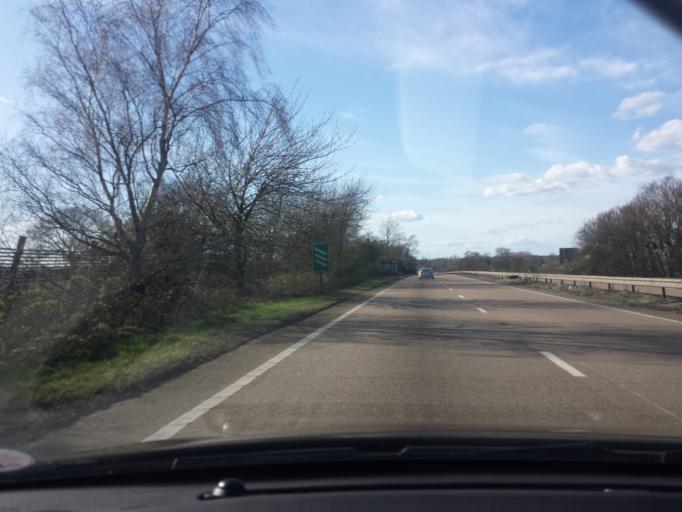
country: GB
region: England
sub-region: Essex
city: Colchester
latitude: 51.9169
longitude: 0.9444
